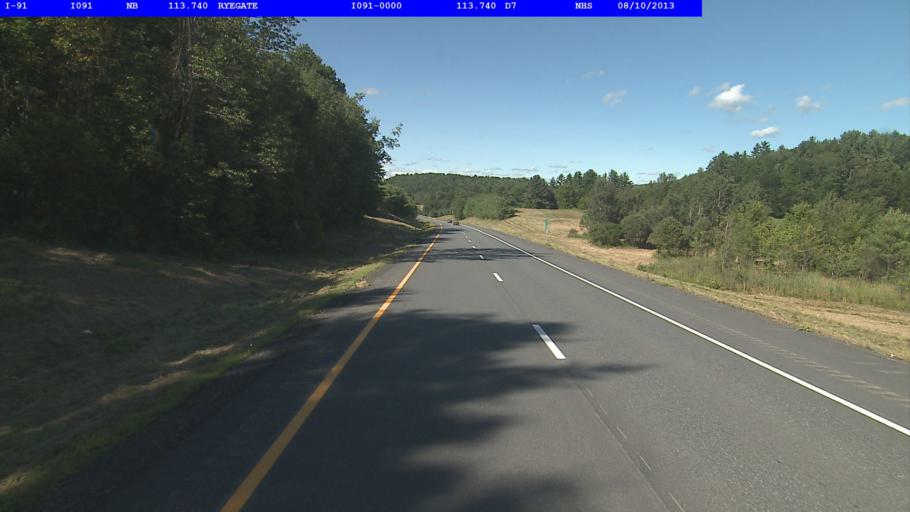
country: US
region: New Hampshire
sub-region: Grafton County
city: Woodsville
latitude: 44.2067
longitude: -72.0683
